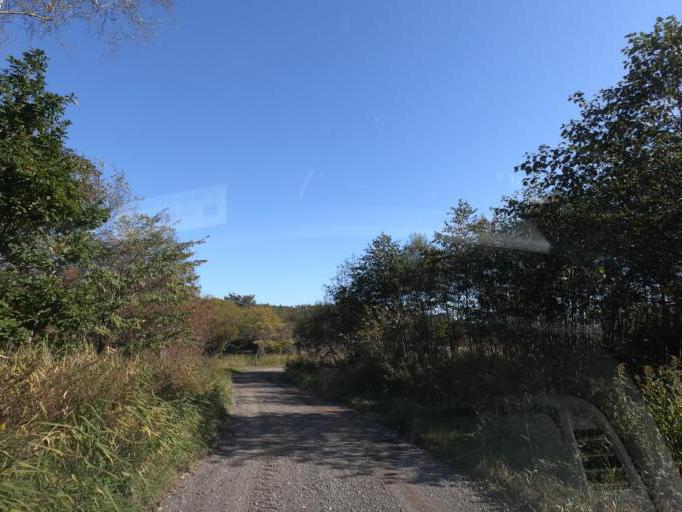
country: JP
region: Hokkaido
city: Obihiro
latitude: 42.7271
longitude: 143.4544
